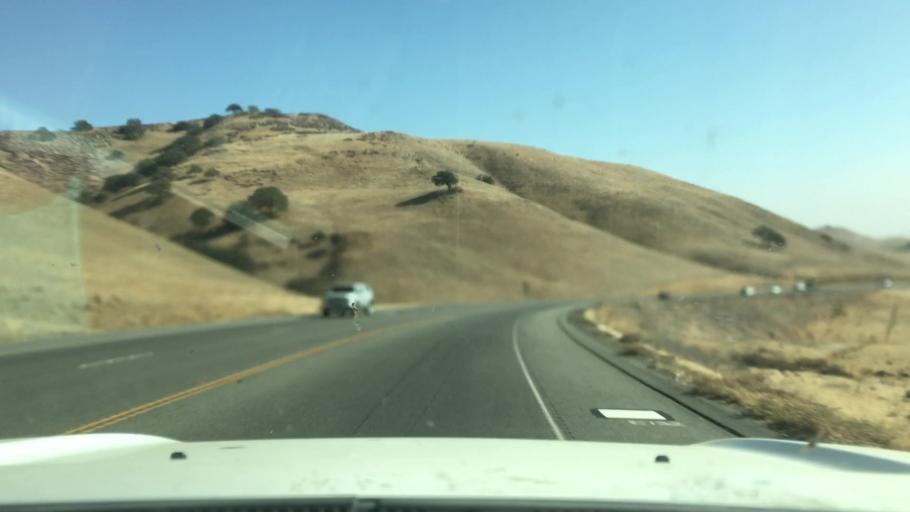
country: US
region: California
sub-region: San Luis Obispo County
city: Shandon
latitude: 35.7427
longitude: -120.2139
